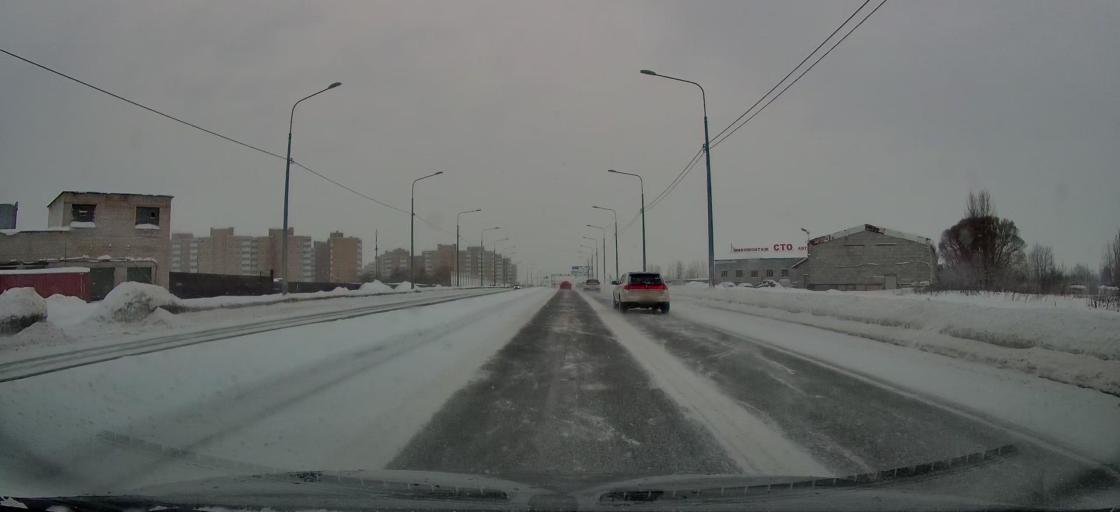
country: RU
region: St.-Petersburg
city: Krasnoye Selo
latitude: 59.7498
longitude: 30.0847
